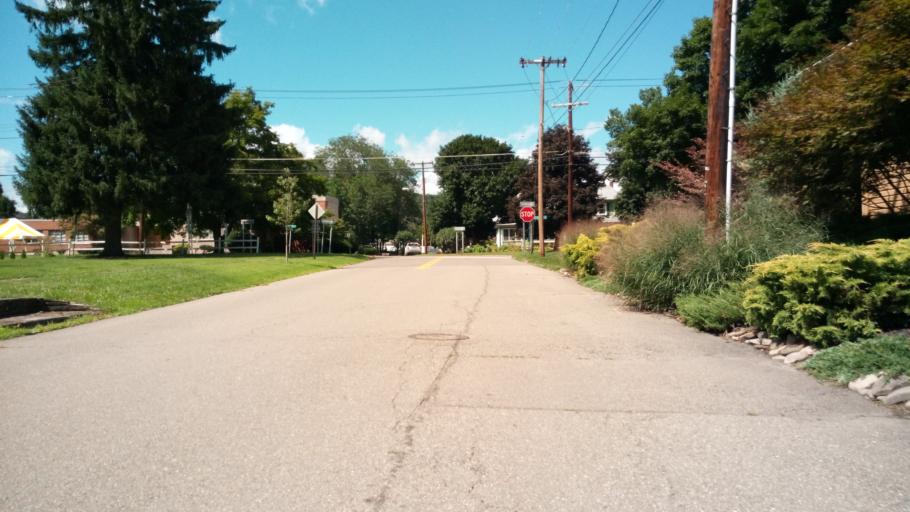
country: US
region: New York
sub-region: Chemung County
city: West Elmira
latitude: 42.0800
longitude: -76.8321
